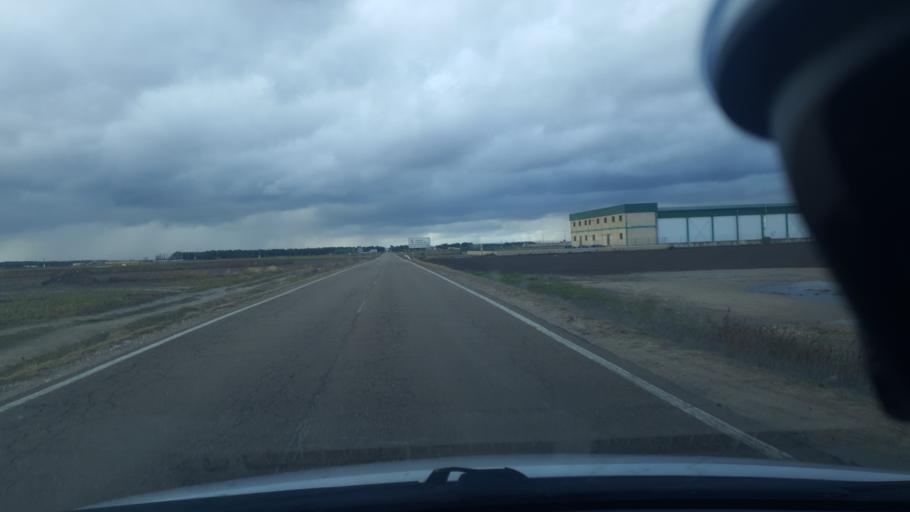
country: ES
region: Castille and Leon
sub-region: Provincia de Segovia
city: Sanchonuno
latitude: 41.2936
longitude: -4.3311
